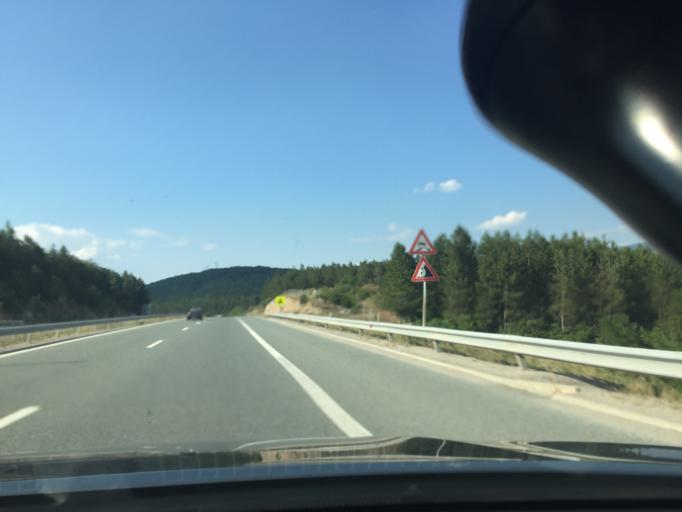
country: BG
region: Pernik
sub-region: Obshtina Pernik
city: Pernik
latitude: 42.5102
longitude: 23.1413
